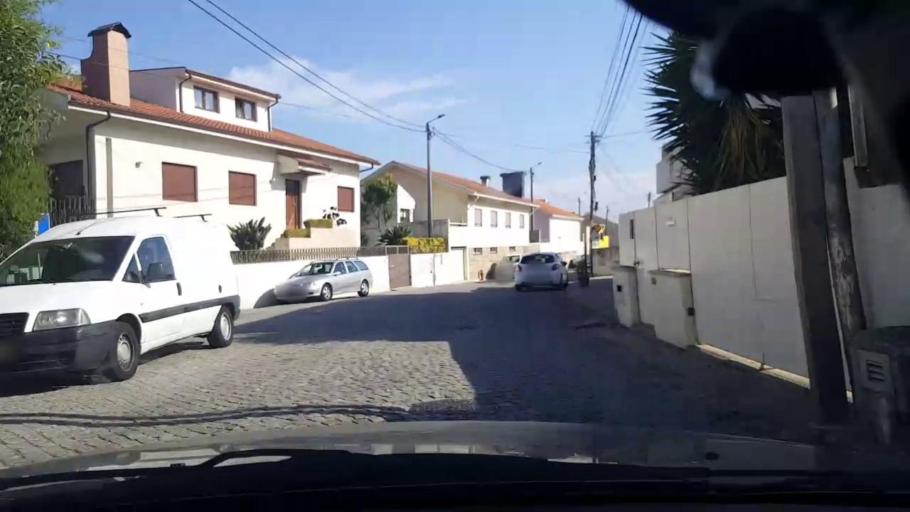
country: PT
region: Porto
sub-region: Maia
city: Gemunde
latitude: 41.2716
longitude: -8.6651
